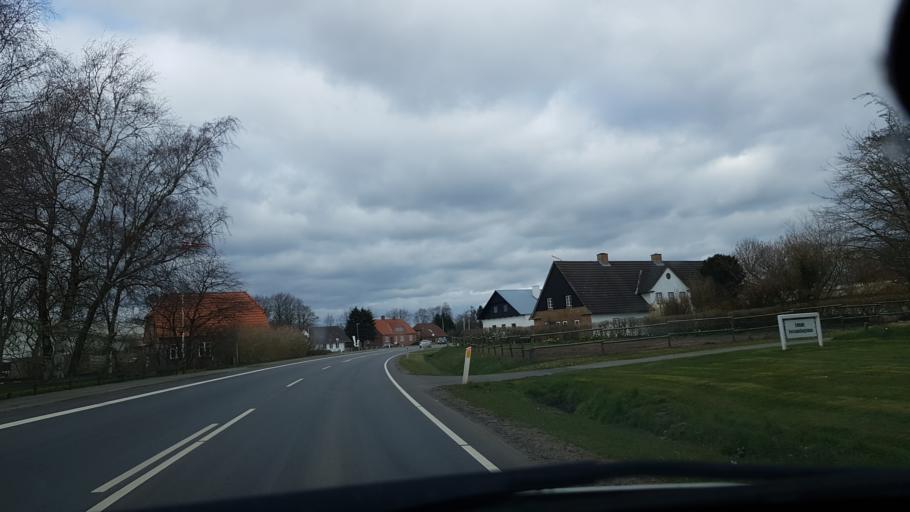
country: DK
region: South Denmark
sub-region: Vejen Kommune
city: Holsted
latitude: 55.4146
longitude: 8.8886
